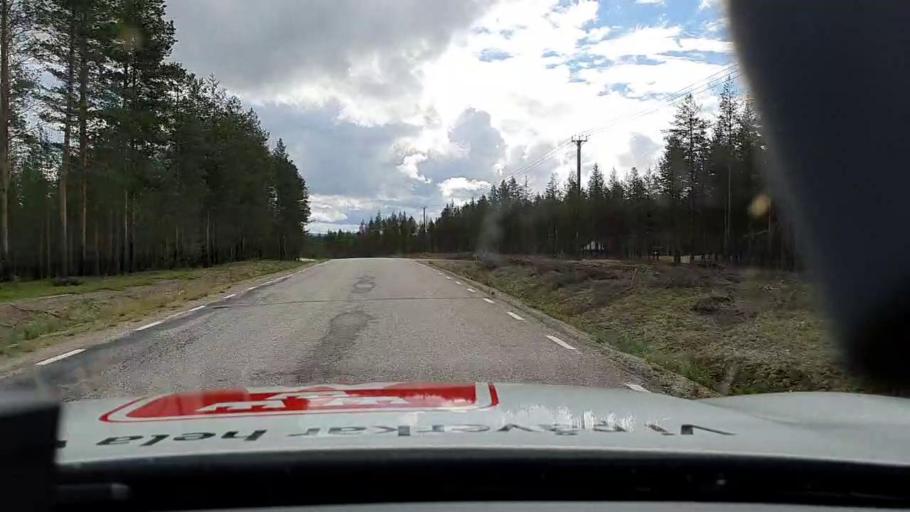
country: SE
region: Norrbotten
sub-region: Overkalix Kommun
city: OEverkalix
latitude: 66.2508
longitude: 22.8789
